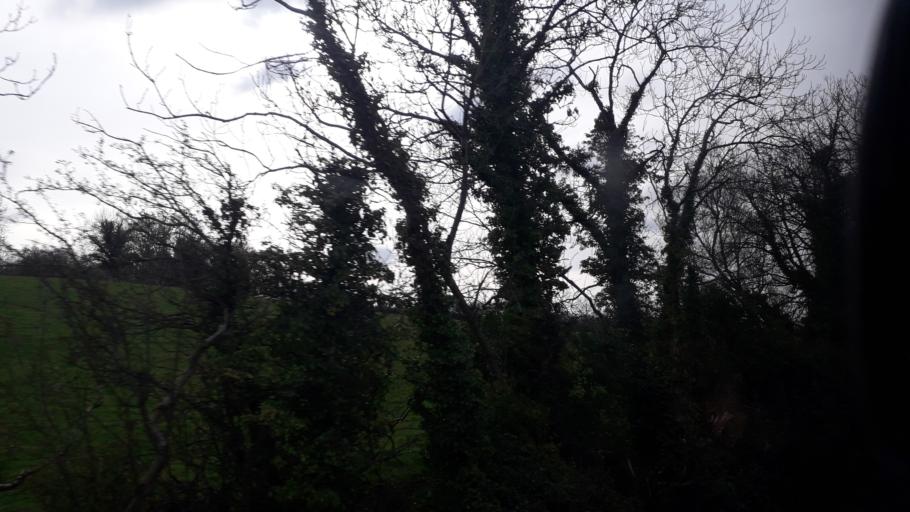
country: IE
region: Leinster
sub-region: Kildare
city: Kilcock
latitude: 53.4138
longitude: -6.6943
